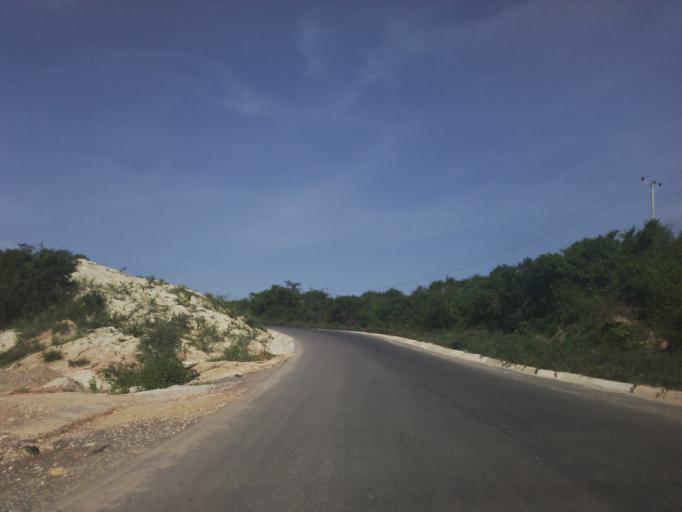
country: TZ
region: Dar es Salaam
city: Magomeni
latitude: -6.7801
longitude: 39.1960
